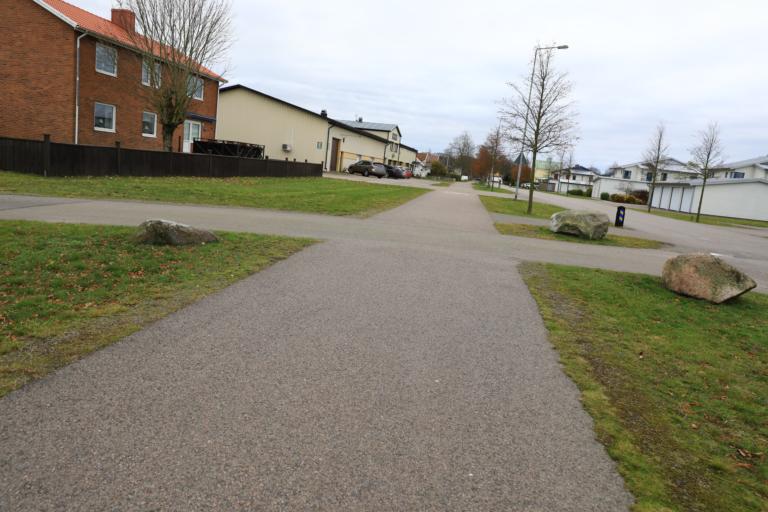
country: SE
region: Halland
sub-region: Varbergs Kommun
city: Tvaaker
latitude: 57.0446
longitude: 12.3971
